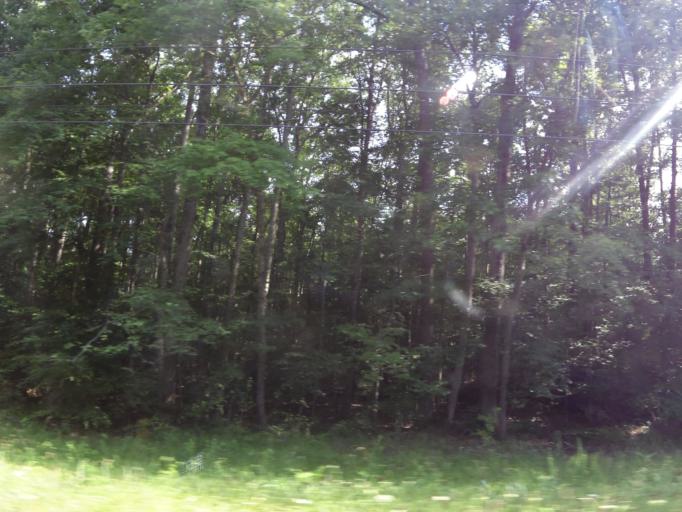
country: US
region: Tennessee
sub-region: Carroll County
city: Bruceton
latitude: 36.0358
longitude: -88.2186
